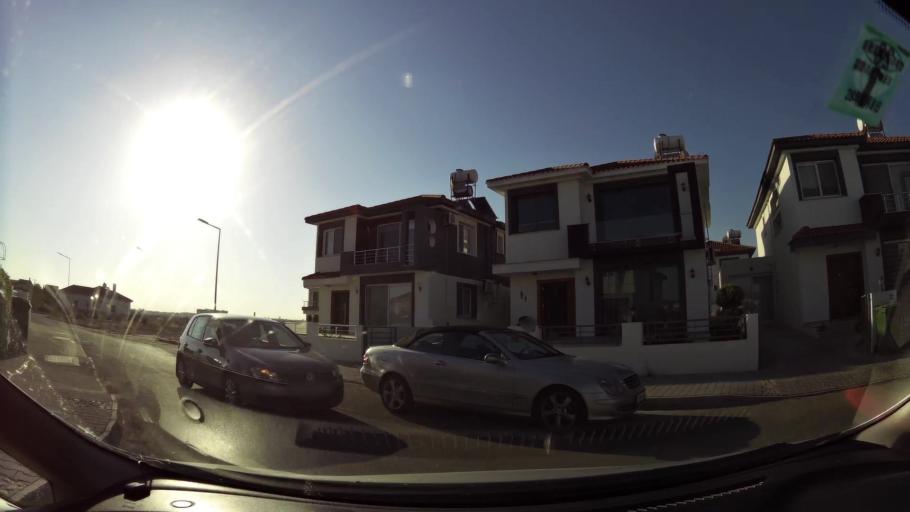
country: CY
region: Lefkosia
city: Nicosia
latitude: 35.2022
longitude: 33.3044
